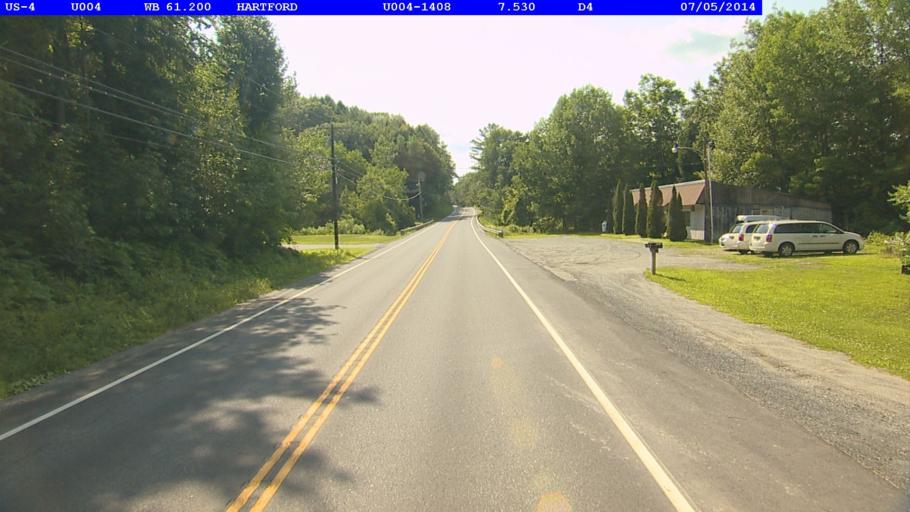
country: US
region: Vermont
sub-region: Windsor County
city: White River Junction
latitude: 43.6630
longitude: -72.3617
